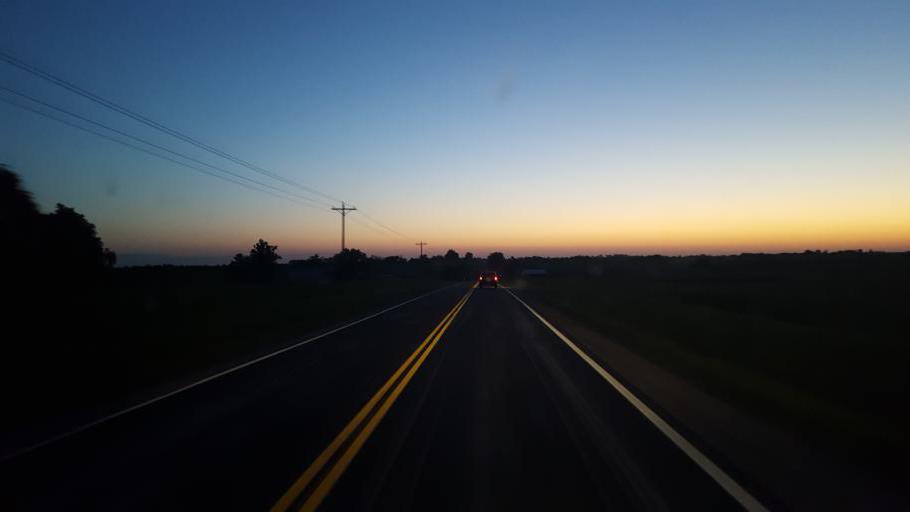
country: US
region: Missouri
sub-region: Mercer County
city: Princeton
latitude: 40.4260
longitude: -93.4850
